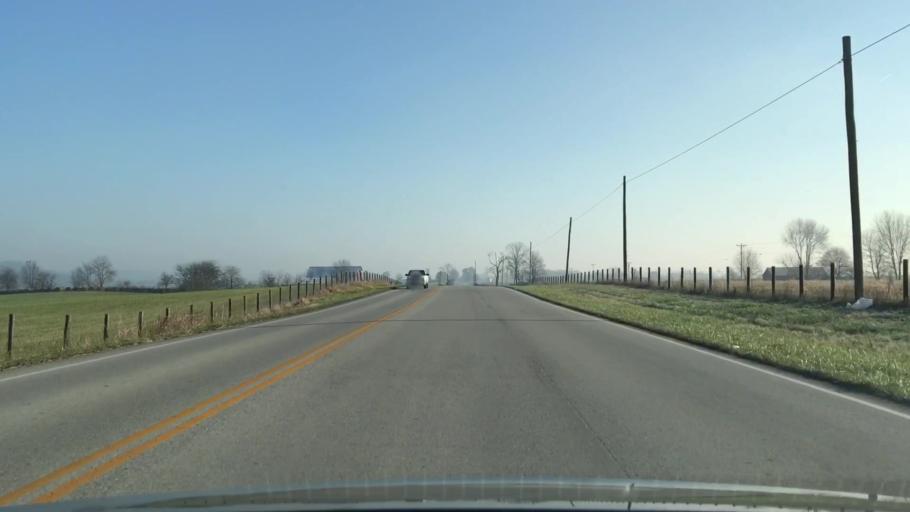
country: US
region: Kentucky
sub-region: Edmonson County
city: Brownsville
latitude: 37.0745
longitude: -86.2568
